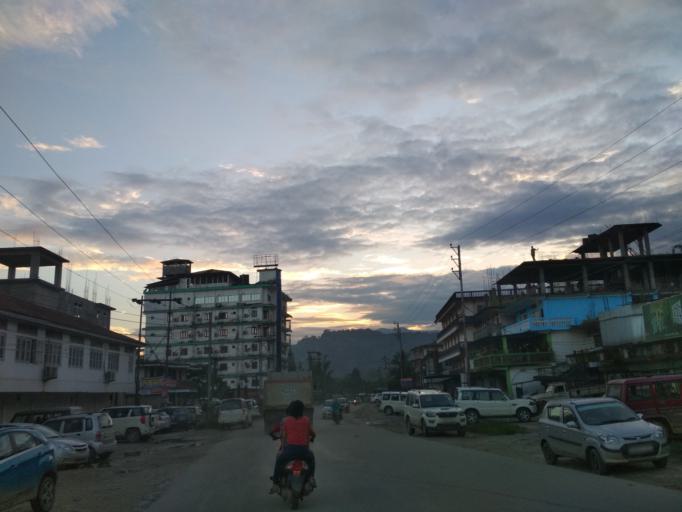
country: IN
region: Arunachal Pradesh
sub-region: Papum Pare
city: Naharlagun
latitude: 27.0978
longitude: 93.6775
